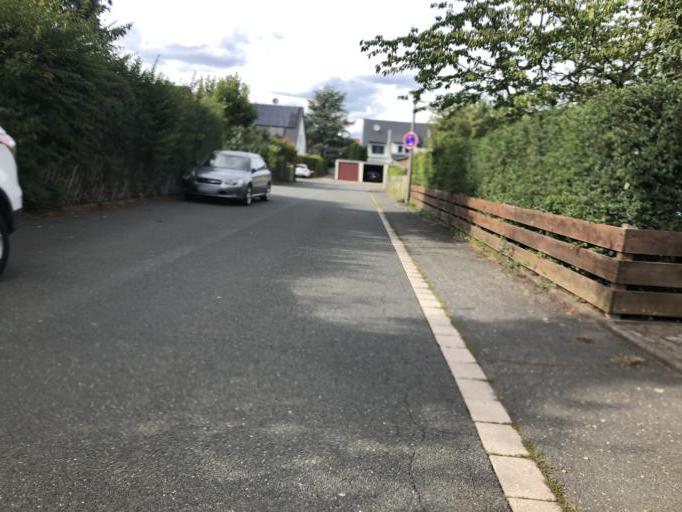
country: DE
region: Bavaria
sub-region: Regierungsbezirk Mittelfranken
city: Obermichelbach
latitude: 49.5438
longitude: 10.9600
